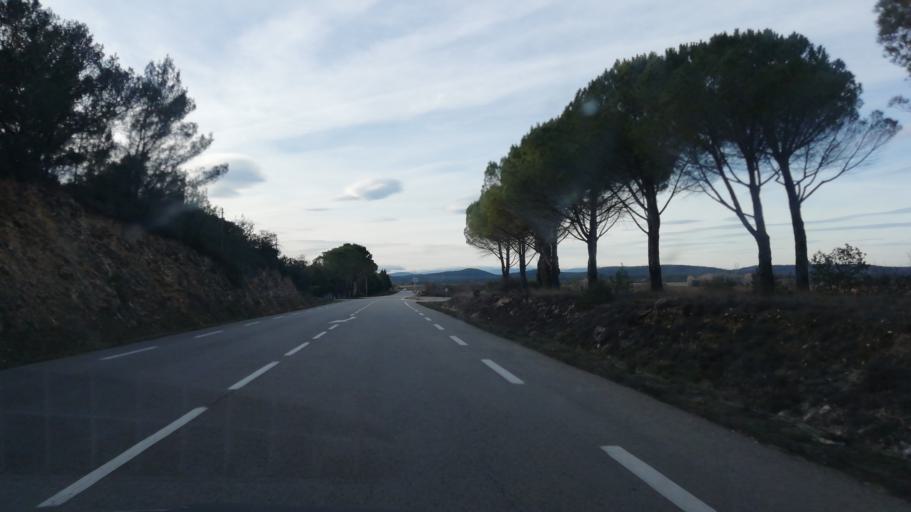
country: FR
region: Languedoc-Roussillon
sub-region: Departement du Gard
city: Saint-Mamert-du-Gard
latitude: 43.8552
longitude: 4.1811
